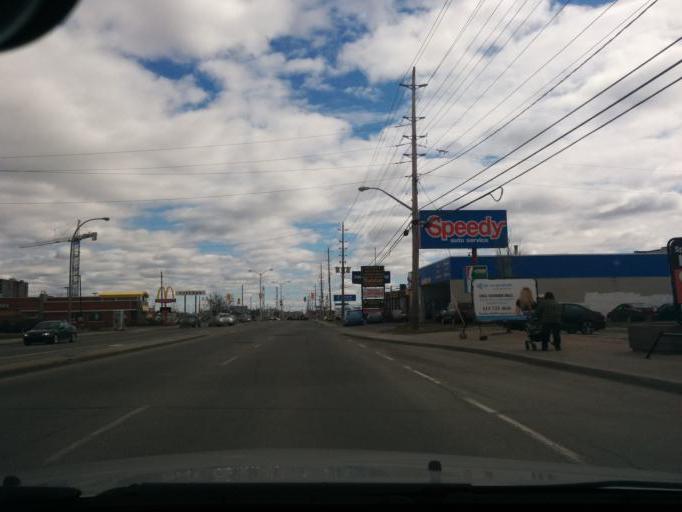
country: CA
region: Ontario
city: Ottawa
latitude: 45.3490
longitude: -75.7325
